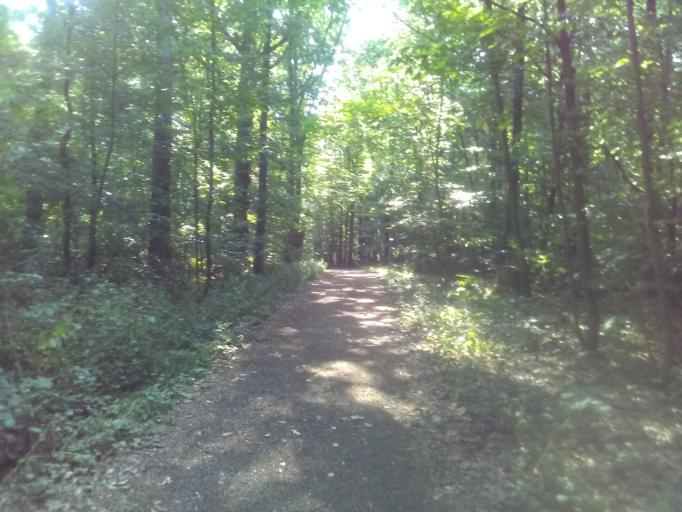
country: DE
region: Bavaria
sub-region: Upper Franconia
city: Bamberg
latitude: 49.8669
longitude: 10.8968
